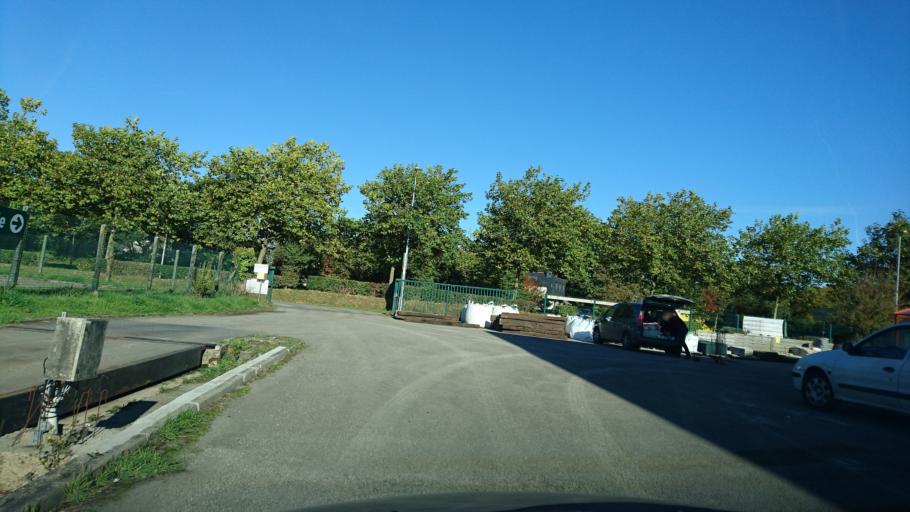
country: FR
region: Brittany
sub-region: Departement du Finistere
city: Saint-Renan
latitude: 48.4256
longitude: -4.6042
